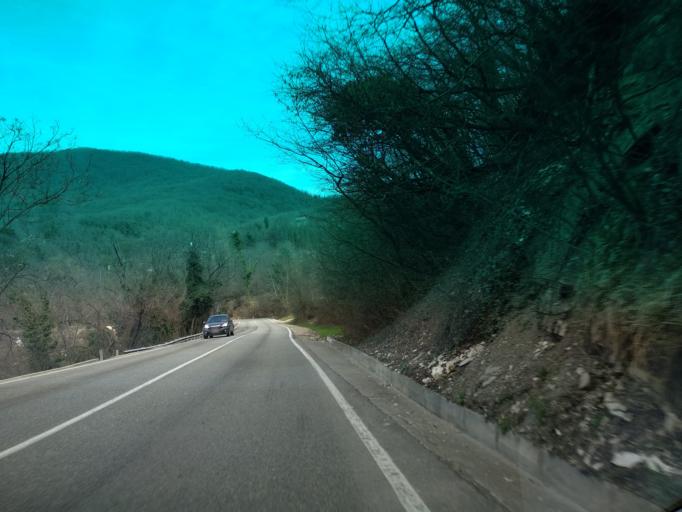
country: RU
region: Krasnodarskiy
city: Shepsi
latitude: 44.0782
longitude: 39.1326
